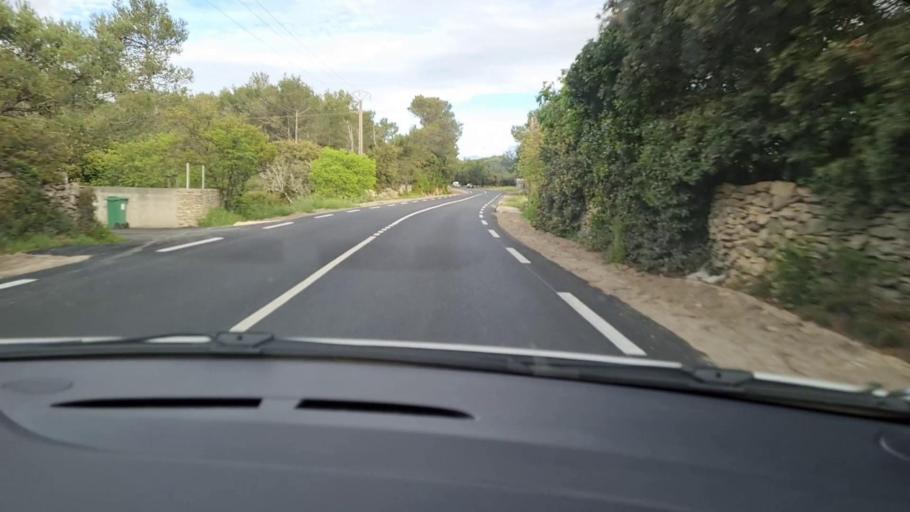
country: FR
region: Languedoc-Roussillon
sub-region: Departement du Gard
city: Caveirac
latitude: 43.8498
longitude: 4.2859
